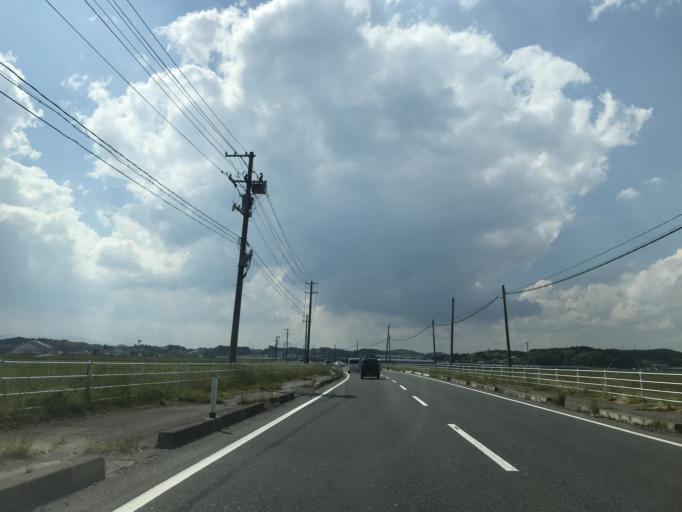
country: JP
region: Miyagi
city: Wakuya
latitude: 38.4743
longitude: 141.1179
